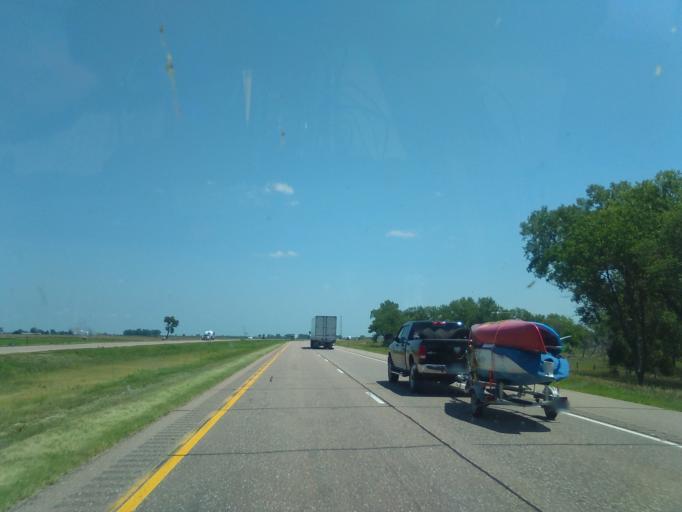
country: US
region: Nebraska
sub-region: Dawson County
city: Gothenburg
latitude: 40.8853
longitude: -100.0897
